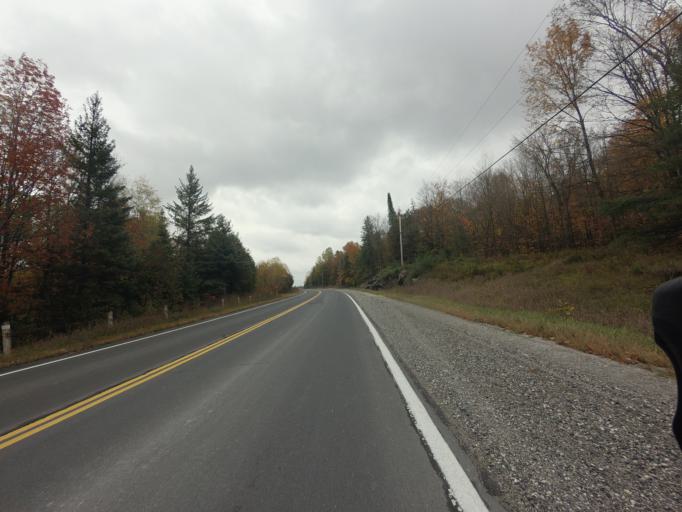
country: CA
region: Ontario
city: Perth
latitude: 45.1157
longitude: -76.4899
